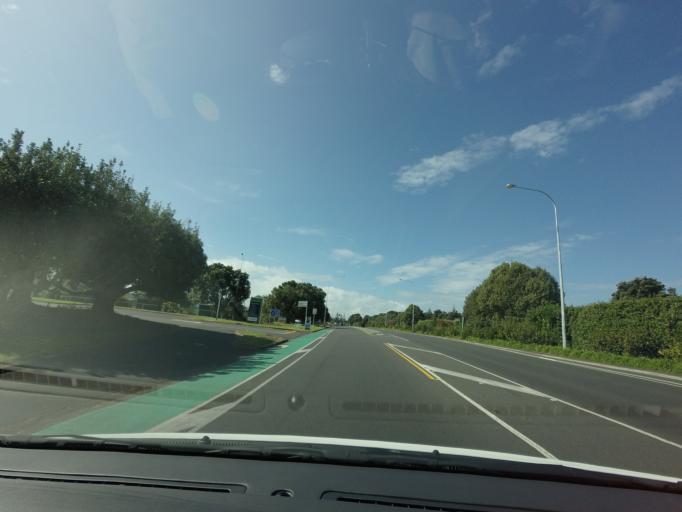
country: NZ
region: Auckland
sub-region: Auckland
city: Rothesay Bay
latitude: -36.5981
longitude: 174.6984
